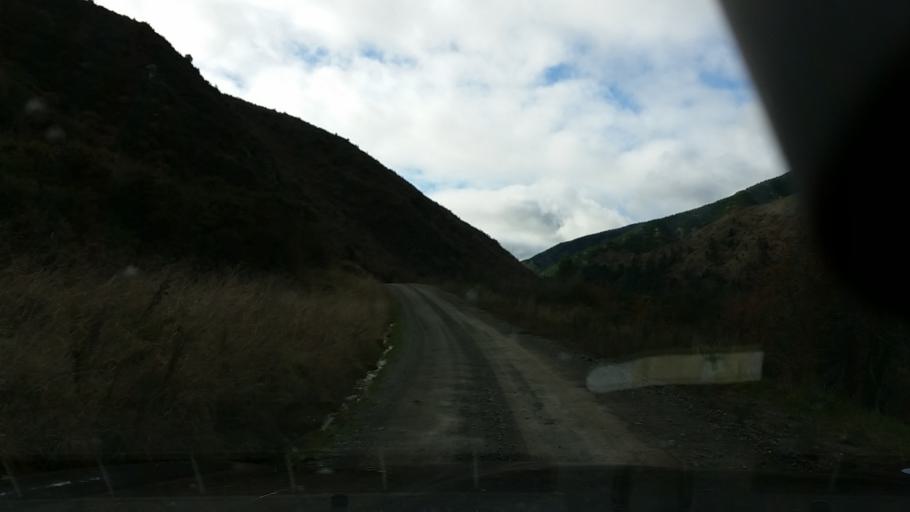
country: NZ
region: Tasman
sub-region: Tasman District
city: Richmond
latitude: -41.7144
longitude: 173.4781
